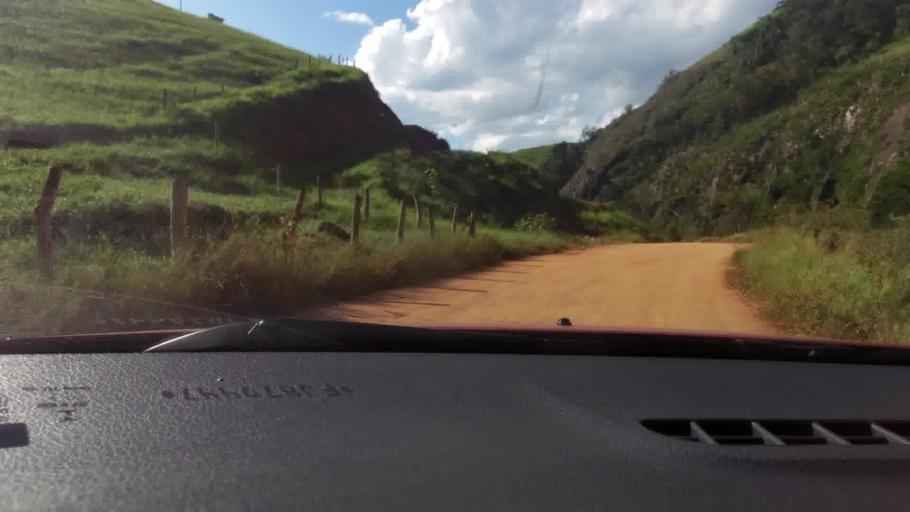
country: BR
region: Espirito Santo
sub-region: Guarapari
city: Guarapari
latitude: -20.5299
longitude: -40.5646
